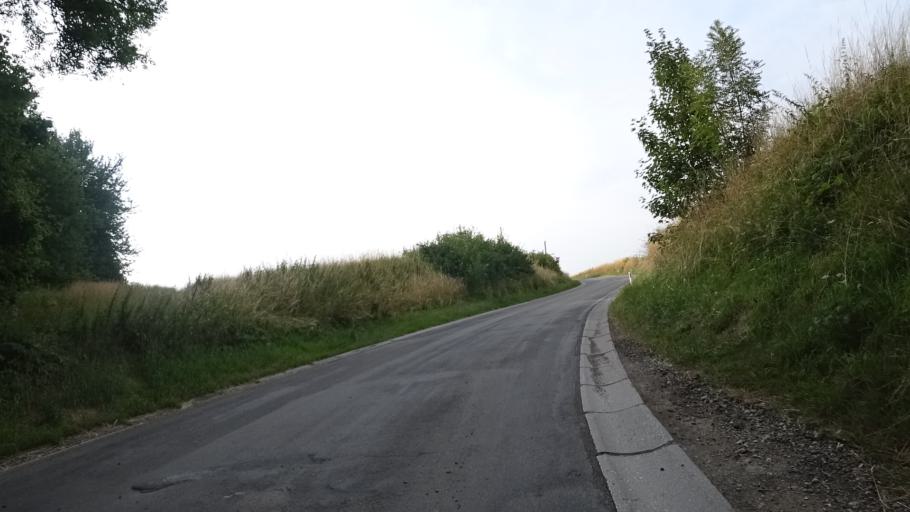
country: BE
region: Wallonia
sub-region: Province du Brabant Wallon
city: Perwez
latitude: 50.5849
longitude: 4.8283
